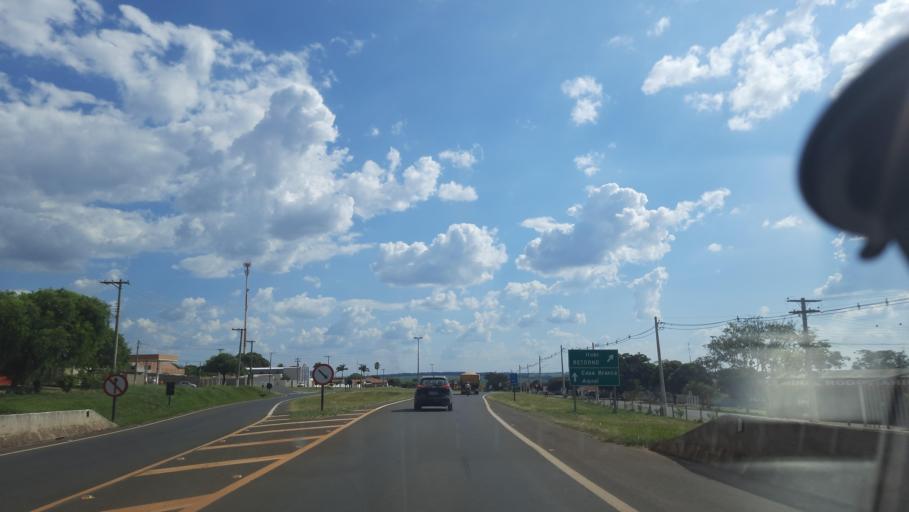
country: BR
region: Sao Paulo
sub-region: Casa Branca
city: Casa Branca
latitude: -21.7345
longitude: -46.9707
